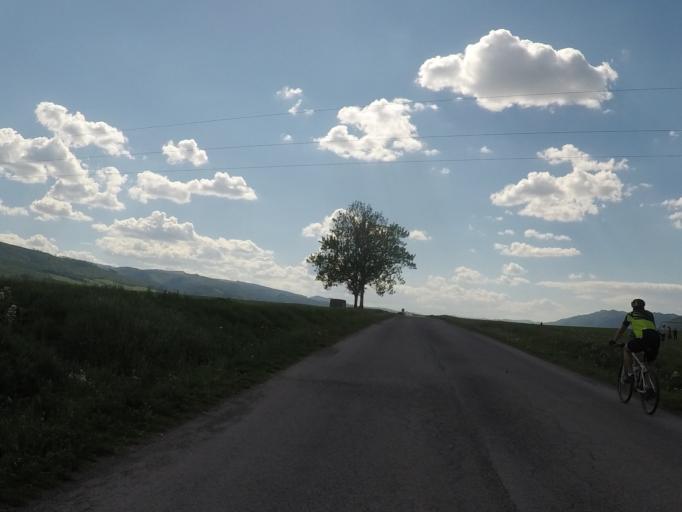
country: SK
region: Presovsky
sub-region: Okres Poprad
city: Poprad
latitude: 48.9945
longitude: 20.3513
